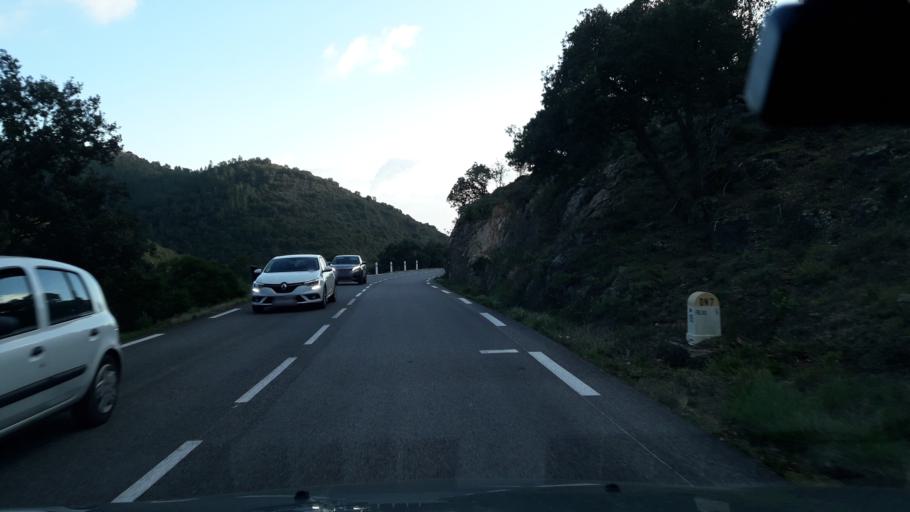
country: FR
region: Provence-Alpes-Cote d'Azur
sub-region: Departement du Var
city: Saint-Raphael
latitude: 43.4982
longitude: 6.7817
